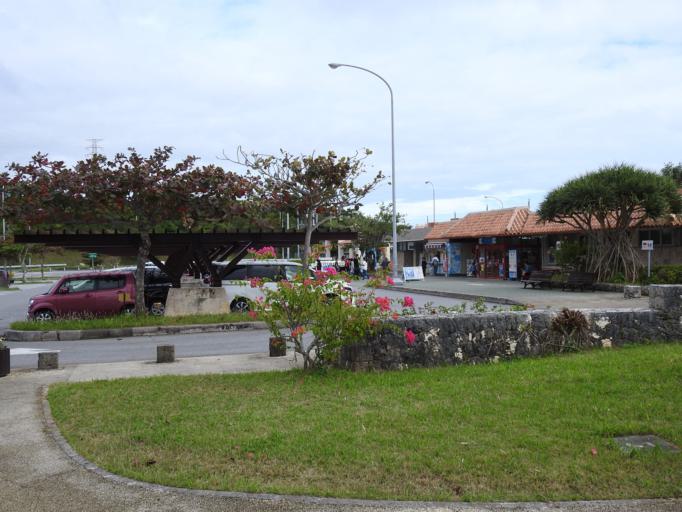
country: JP
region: Okinawa
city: Ishikawa
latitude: 26.4608
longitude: 127.8700
